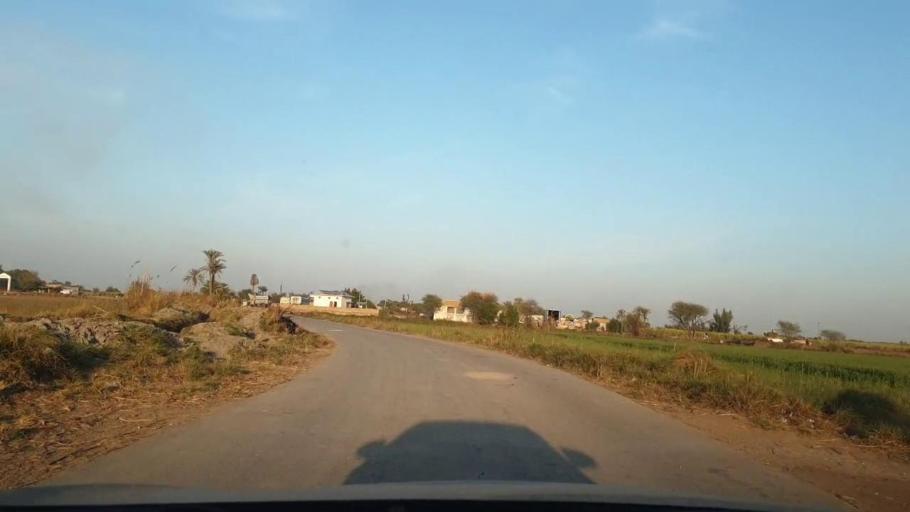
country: PK
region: Sindh
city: Tando Adam
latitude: 25.6181
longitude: 68.6866
